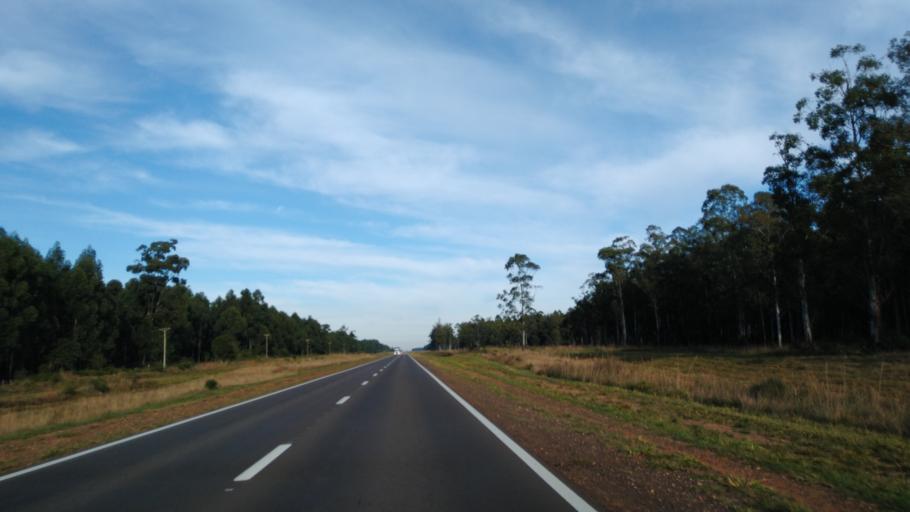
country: AR
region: Corrientes
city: Yapeyu
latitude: -29.4347
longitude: -56.8829
